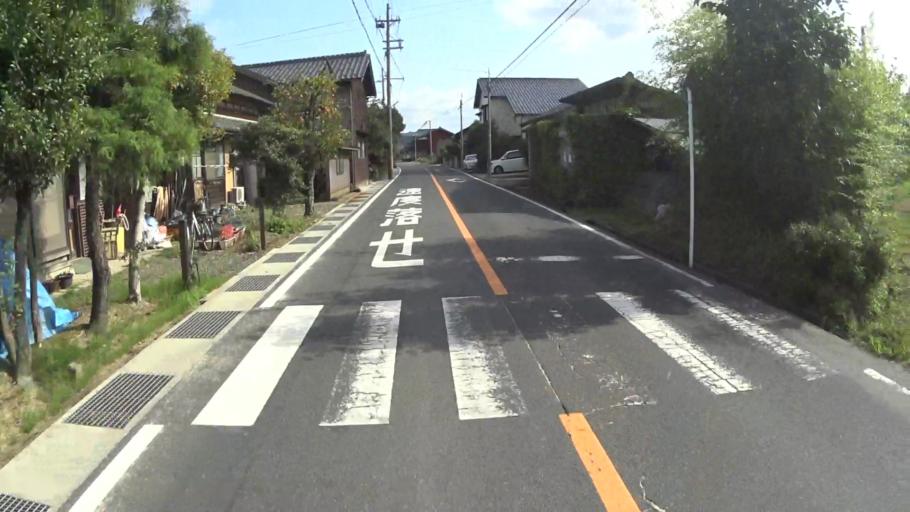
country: JP
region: Kyoto
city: Miyazu
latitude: 35.5995
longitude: 135.0934
